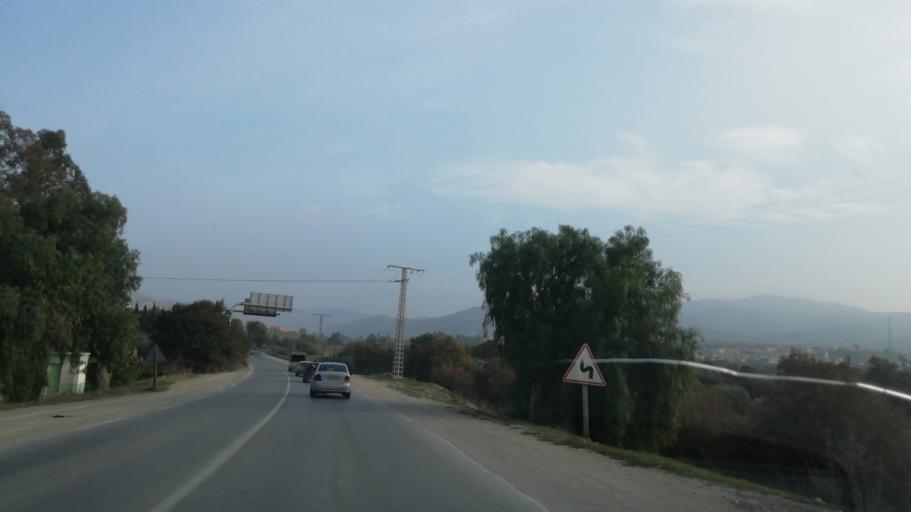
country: DZ
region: Mascara
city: Bou Hanifia el Hamamat
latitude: 35.4683
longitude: -0.0098
